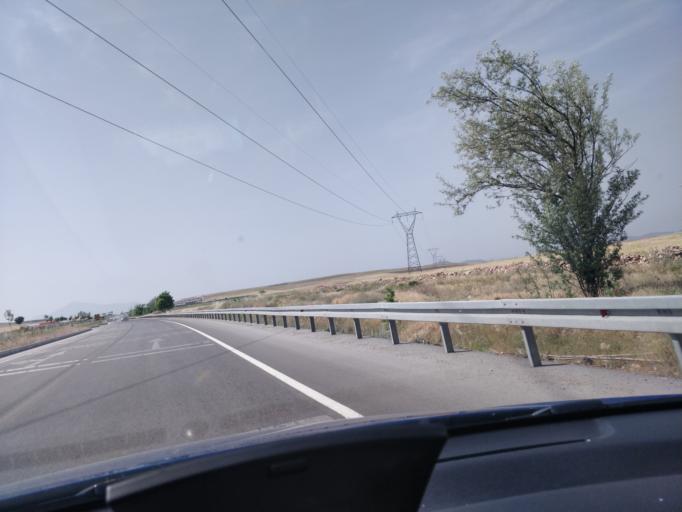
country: TR
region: Konya
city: Cumra
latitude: 37.4489
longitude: 32.7238
